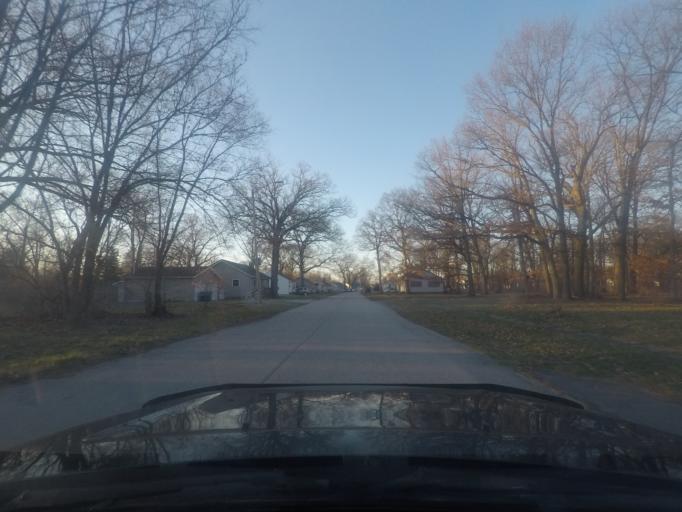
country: US
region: Indiana
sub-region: LaPorte County
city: Kingsford Heights
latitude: 41.4783
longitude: -86.6970
